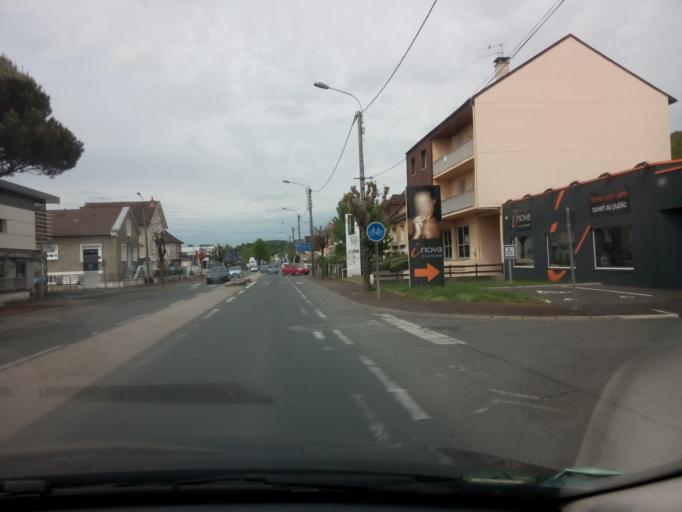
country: FR
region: Limousin
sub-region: Departement de la Correze
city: Brive-la-Gaillarde
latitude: 45.1647
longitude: 1.5074
